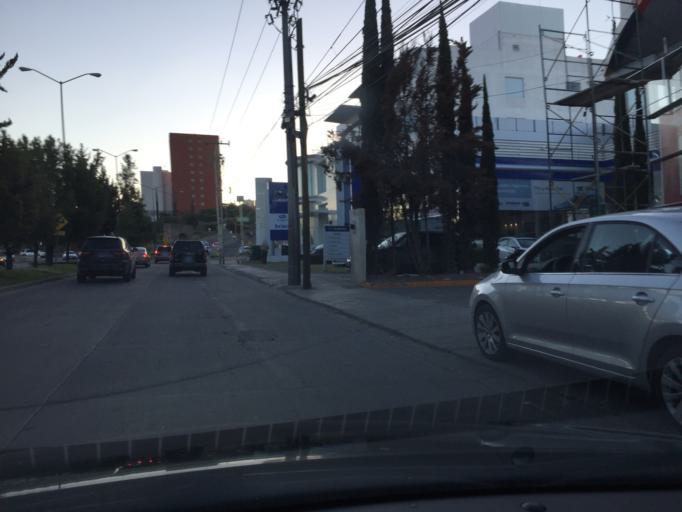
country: MX
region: Guanajuato
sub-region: Leon
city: La Ermita
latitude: 21.1590
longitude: -101.6979
